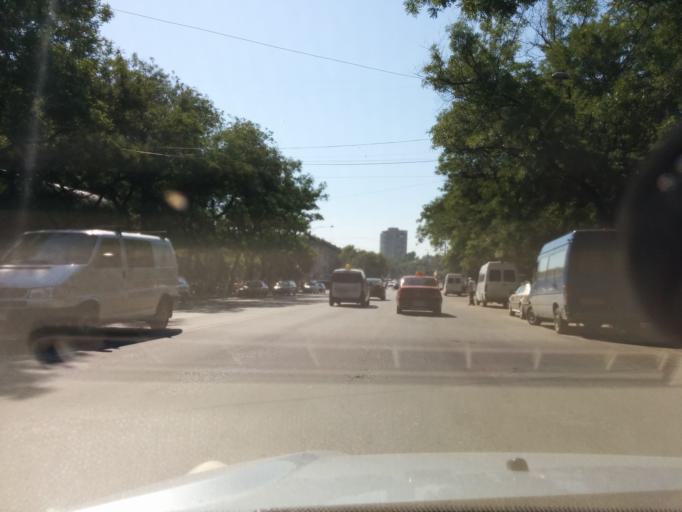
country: MD
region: Chisinau
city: Chisinau
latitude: 47.0124
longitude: 28.8563
